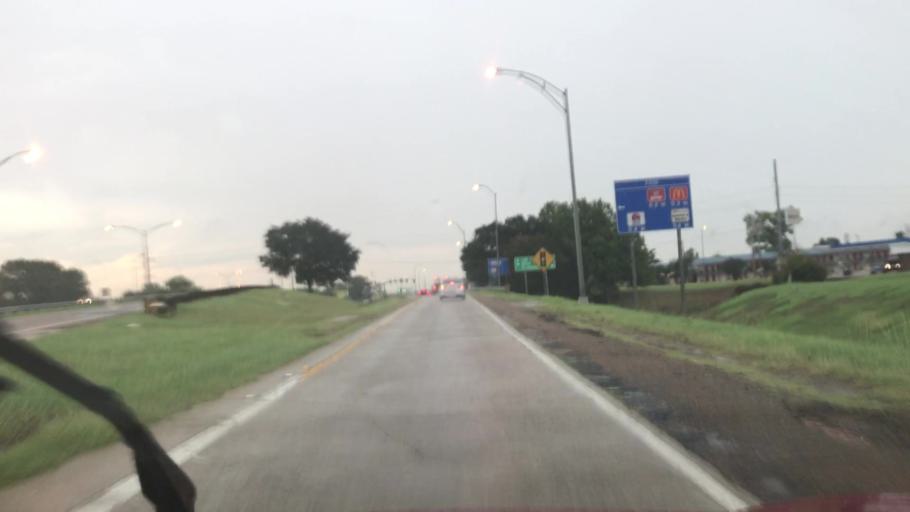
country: US
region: Louisiana
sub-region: Bossier Parish
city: Bossier City
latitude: 32.5277
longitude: -93.6769
